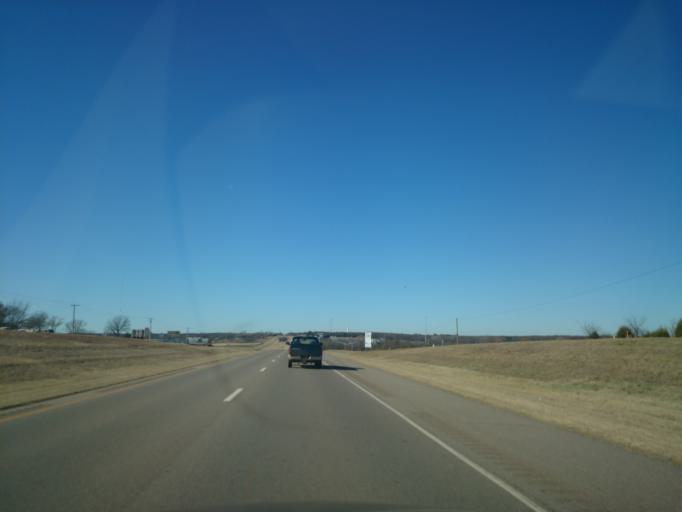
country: US
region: Oklahoma
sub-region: Payne County
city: Stillwater
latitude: 36.1162
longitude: -97.1648
